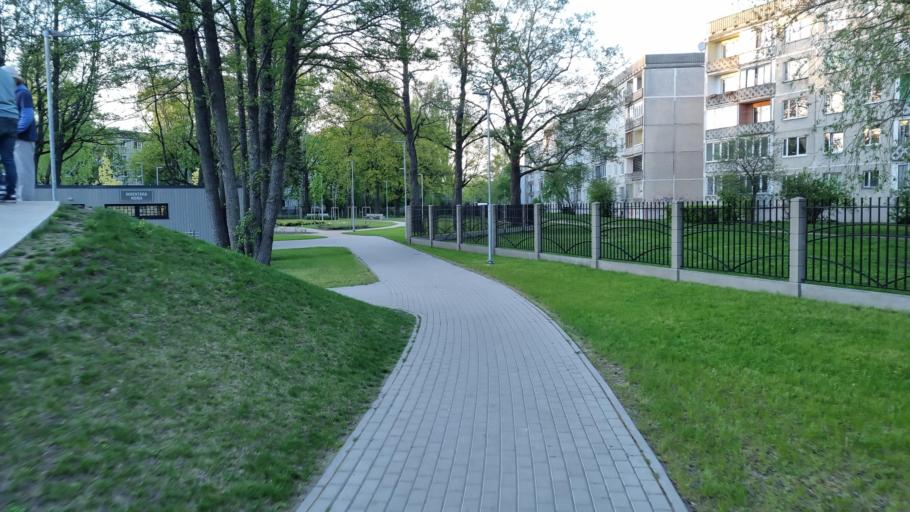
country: LV
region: Marupe
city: Marupe
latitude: 56.9561
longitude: 24.0035
